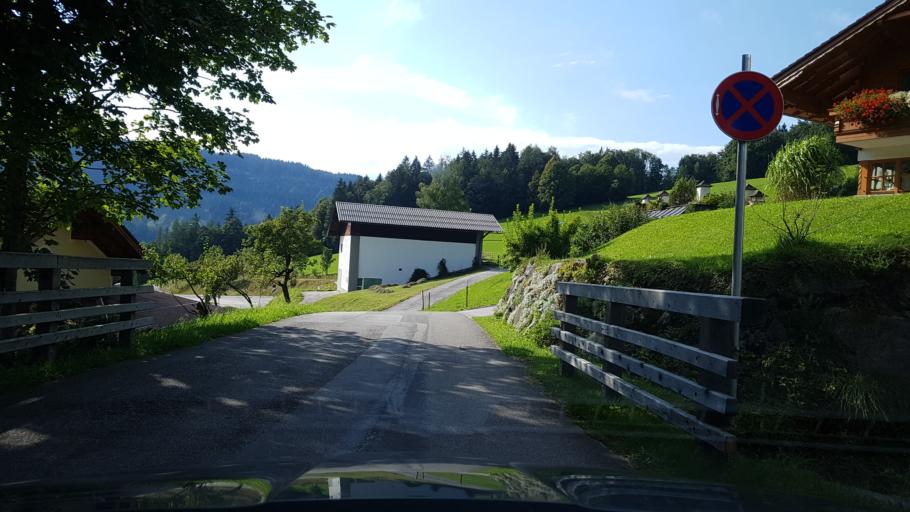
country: AT
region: Salzburg
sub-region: Politischer Bezirk Hallein
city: Krispl
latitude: 47.7026
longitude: 13.2181
